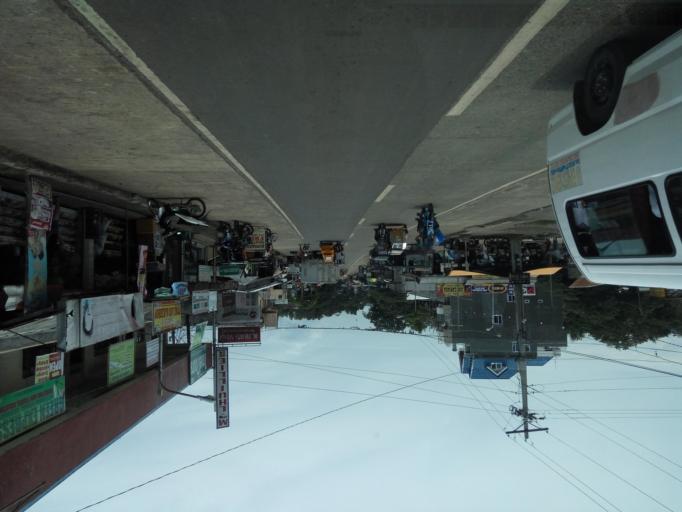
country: PH
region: Cagayan Valley
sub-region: Province of Quirino
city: Diffun
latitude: 16.5940
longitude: 121.5023
